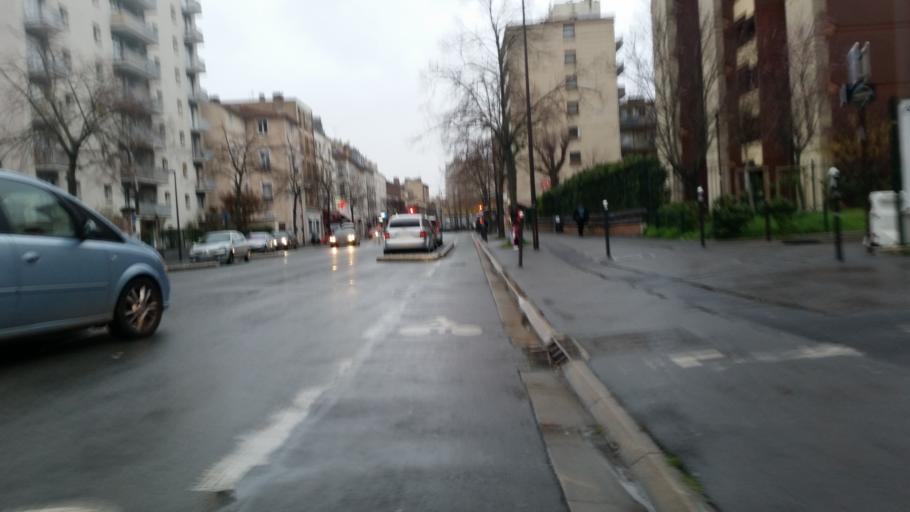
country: FR
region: Ile-de-France
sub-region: Departement du Val-de-Marne
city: Ivry-sur-Seine
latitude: 48.8150
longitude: 2.3838
